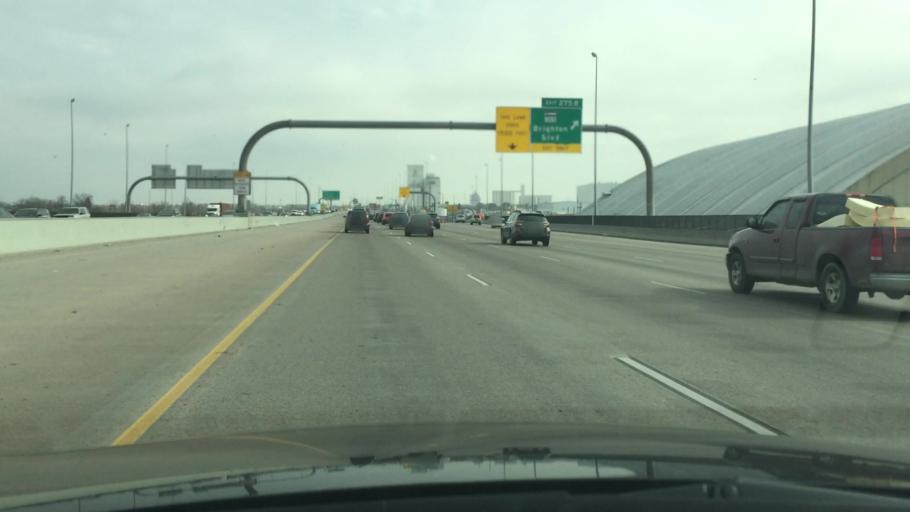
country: US
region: Colorado
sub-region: Denver County
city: Denver
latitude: 39.7797
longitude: -104.9720
